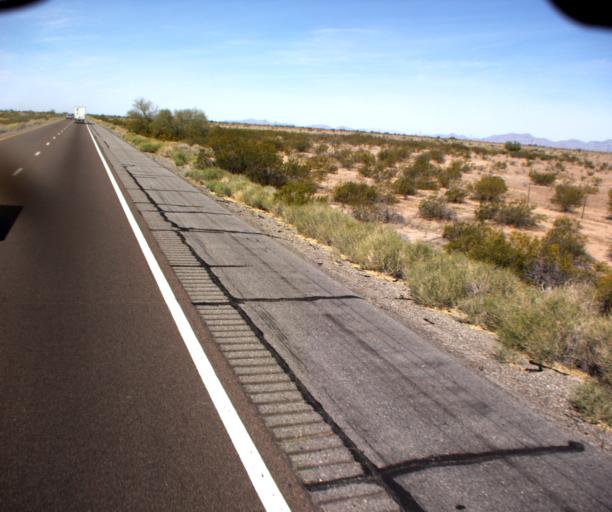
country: US
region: Arizona
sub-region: La Paz County
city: Salome
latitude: 33.5538
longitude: -113.2510
